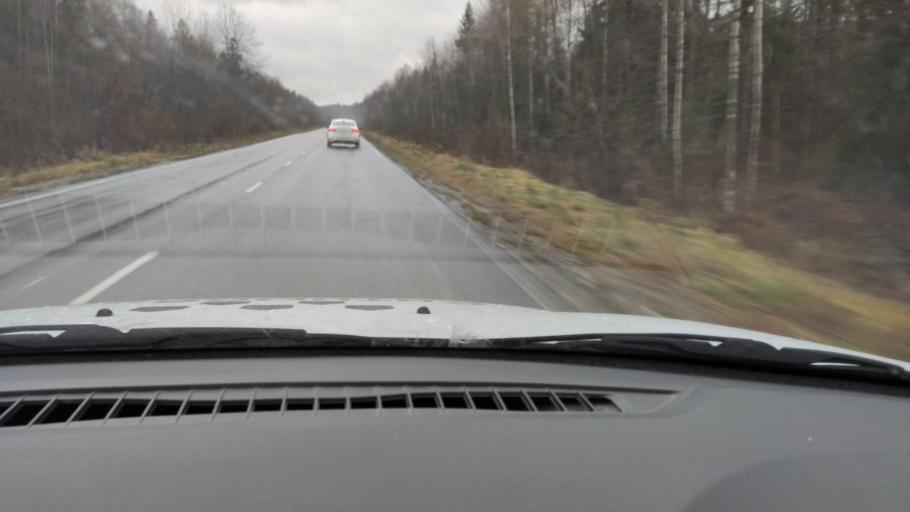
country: RU
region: Perm
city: Novyye Lyady
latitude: 58.0248
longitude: 56.6356
